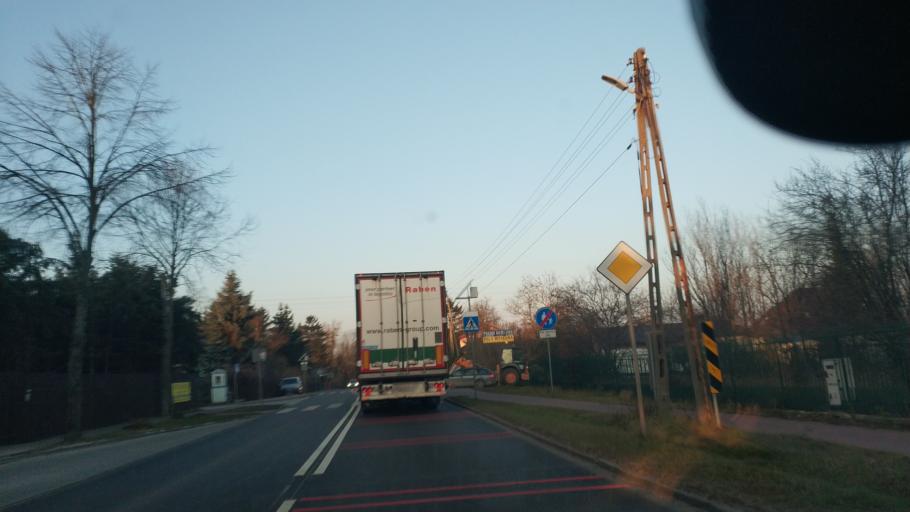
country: PL
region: Masovian Voivodeship
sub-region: Powiat grodziski
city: Milanowek
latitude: 52.0880
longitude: 20.6799
